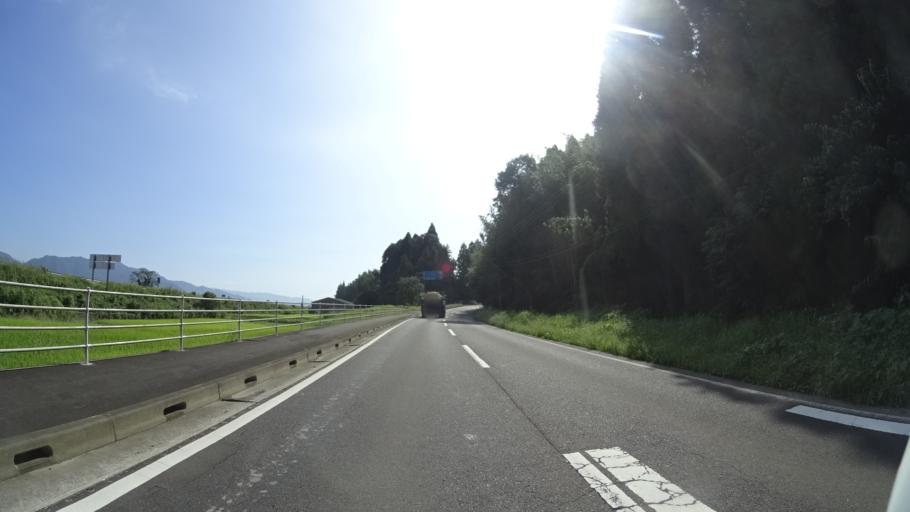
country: JP
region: Miyazaki
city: Kobayashi
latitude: 32.0366
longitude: 130.8195
